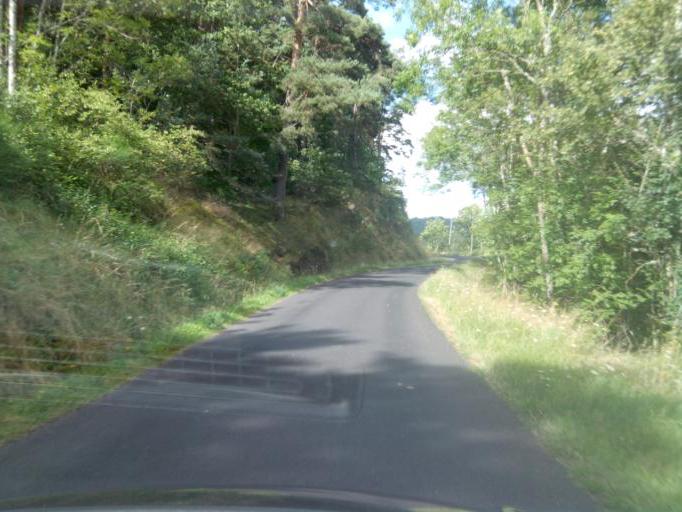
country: FR
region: Auvergne
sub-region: Departement de la Haute-Loire
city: Retournac
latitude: 45.1996
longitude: 3.9776
